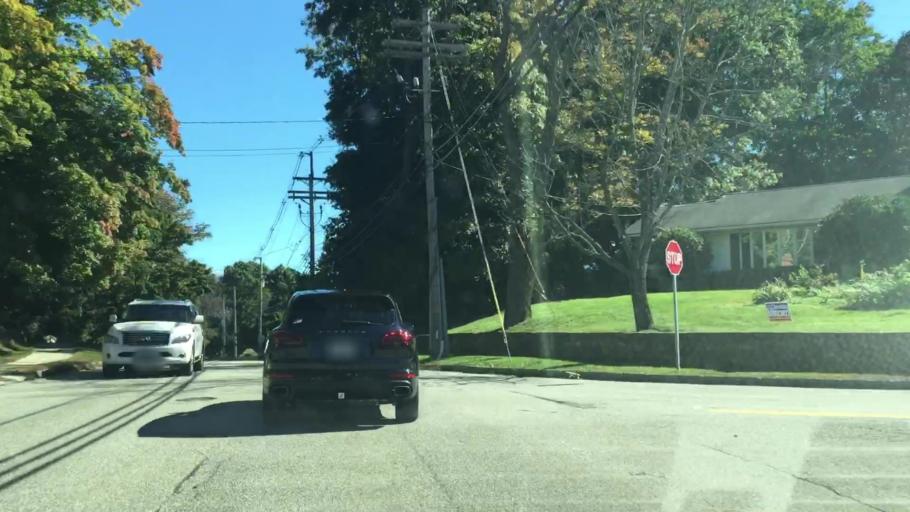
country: US
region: Massachusetts
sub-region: Essex County
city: North Andover
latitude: 42.6825
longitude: -71.1105
